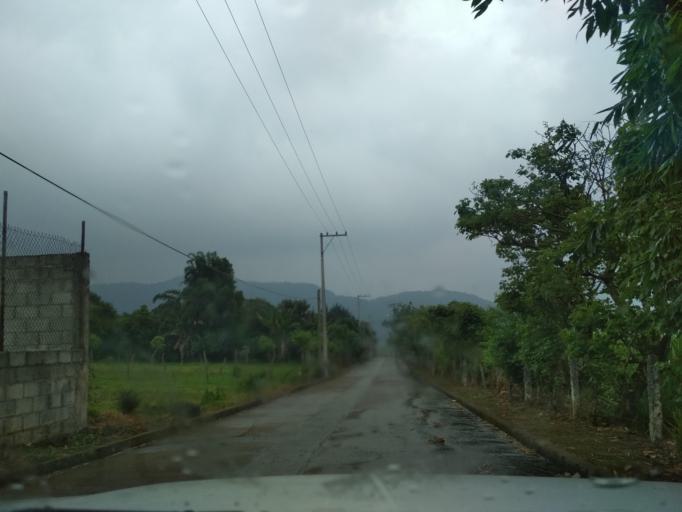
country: MX
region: Veracruz
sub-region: Mariano Escobedo
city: Chicola
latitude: 18.8993
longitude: -97.1171
